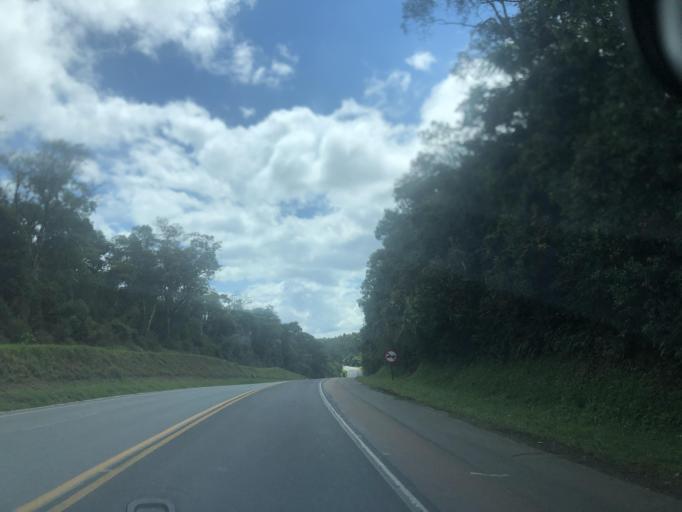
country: BR
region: Santa Catarina
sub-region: Mafra
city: Mafra
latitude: -26.1786
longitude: -49.8614
